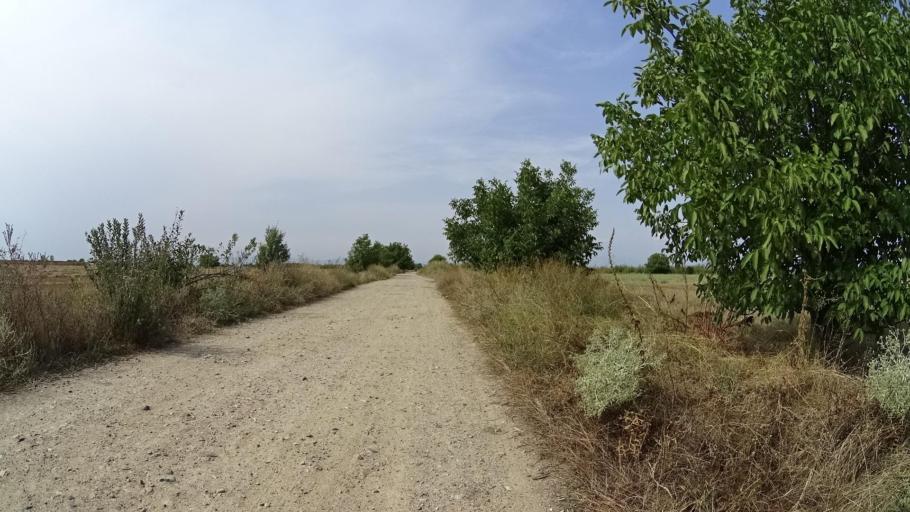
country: BG
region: Plovdiv
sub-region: Obshtina Kaloyanovo
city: Kaloyanovo
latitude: 42.2753
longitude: 24.8006
